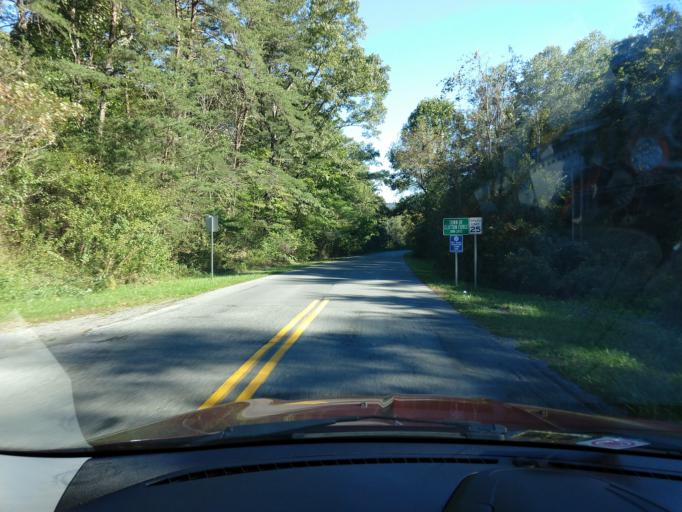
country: US
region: Virginia
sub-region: Alleghany County
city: Clifton Forge
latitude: 37.8281
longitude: -79.8343
